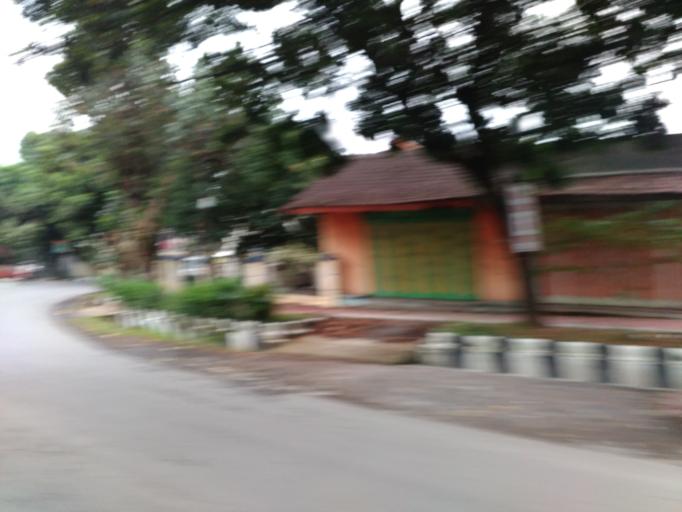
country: ID
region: Central Java
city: Boyolali
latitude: -7.5156
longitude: 110.5941
